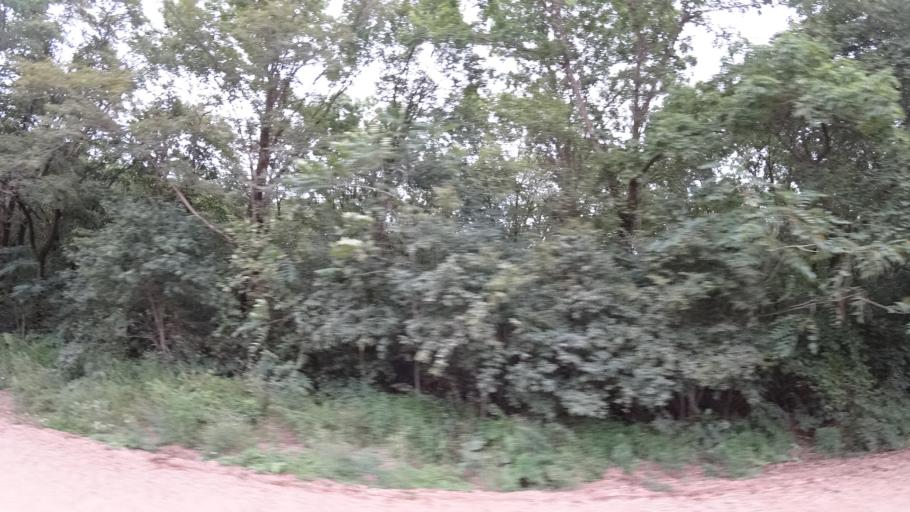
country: RU
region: Primorskiy
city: Rettikhovka
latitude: 44.2490
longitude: 132.6967
